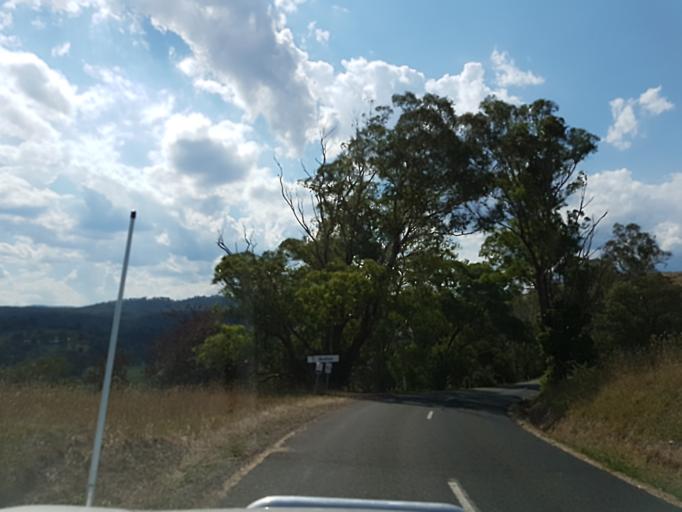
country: AU
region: Victoria
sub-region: East Gippsland
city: Lakes Entrance
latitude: -37.5006
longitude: 148.1844
